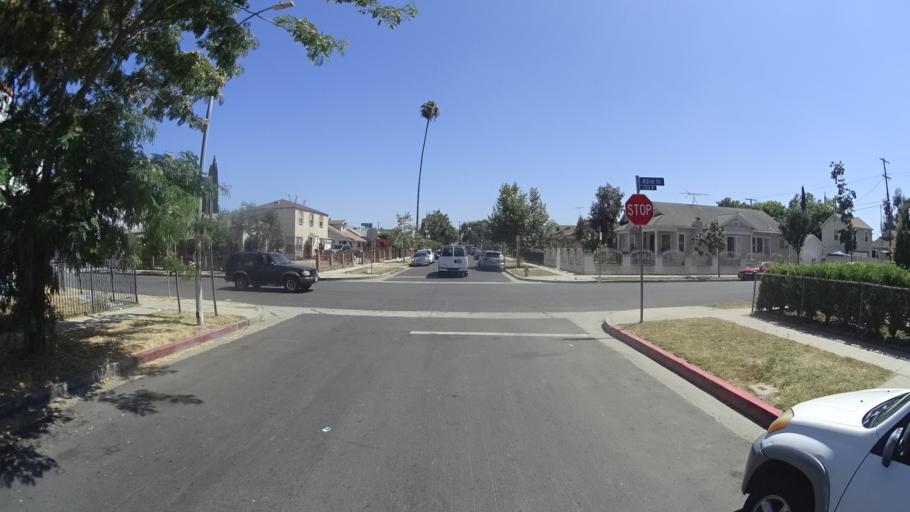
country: US
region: California
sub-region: Los Angeles County
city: View Park-Windsor Hills
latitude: 34.0057
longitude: -118.2948
